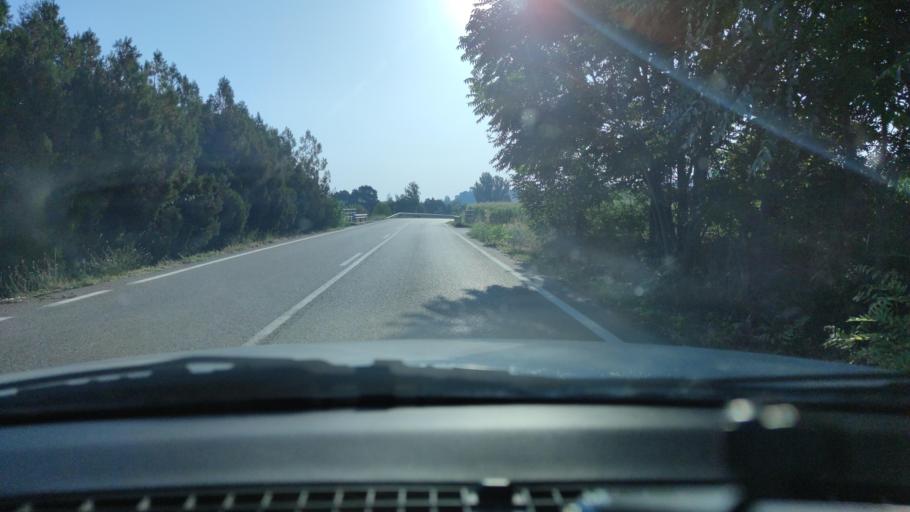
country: ES
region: Catalonia
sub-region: Provincia de Lleida
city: Balaguer
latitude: 41.7993
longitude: 0.8287
